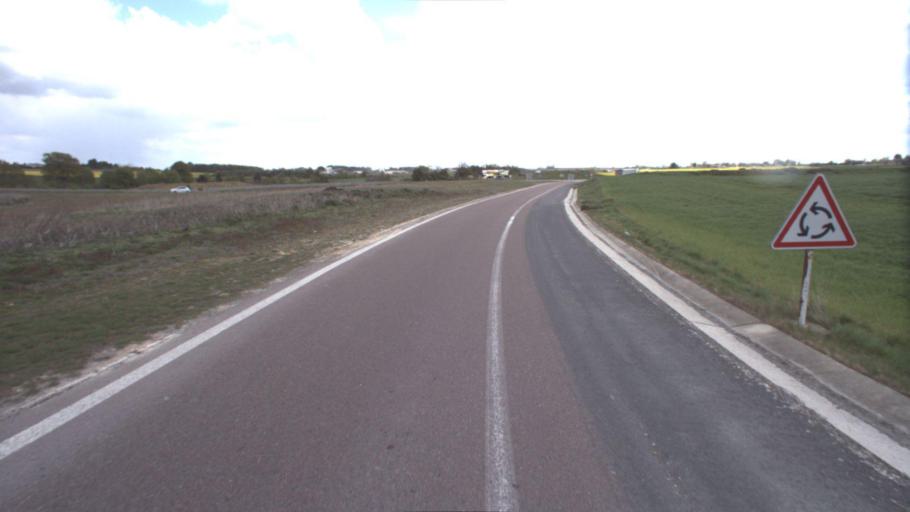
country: FR
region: Ile-de-France
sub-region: Departement de Seine-et-Marne
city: Jouy-le-Chatel
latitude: 48.6840
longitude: 3.1031
